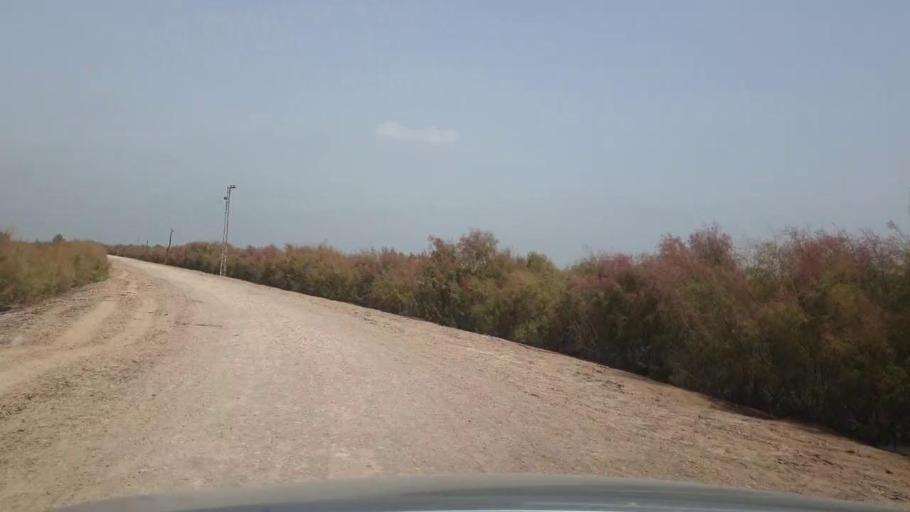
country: PK
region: Sindh
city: Garhi Yasin
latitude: 27.9539
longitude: 68.3658
